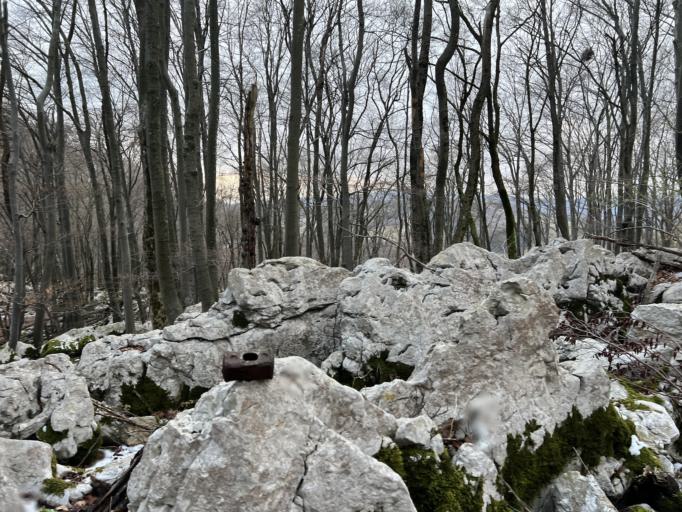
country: SI
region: Kanal
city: Kanal
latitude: 46.0687
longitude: 13.6742
